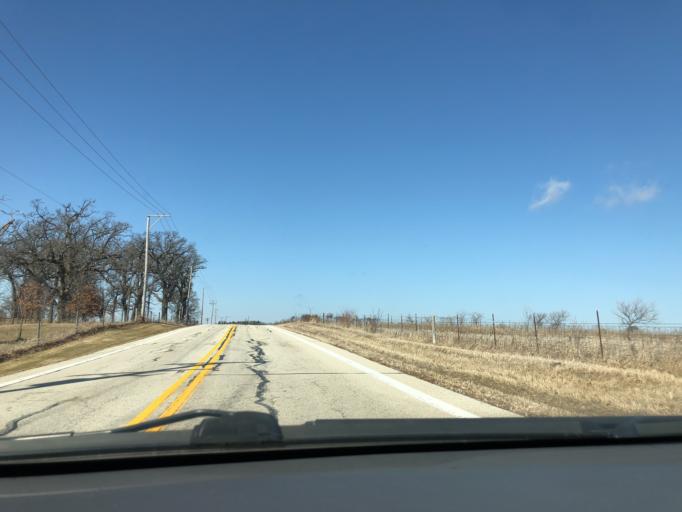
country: US
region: Illinois
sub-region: Kane County
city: Hampshire
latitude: 42.1330
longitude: -88.5298
